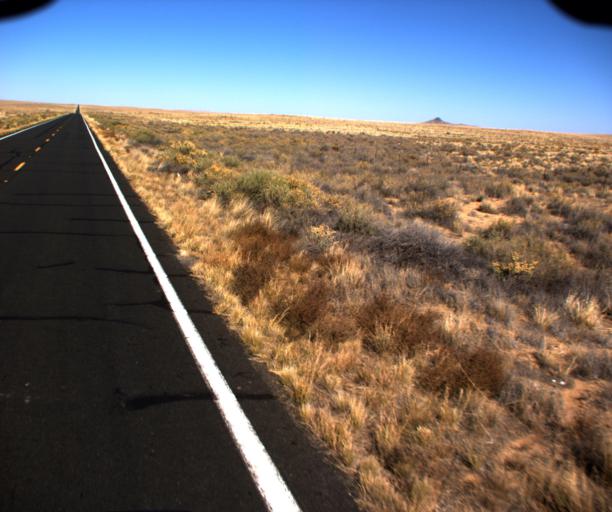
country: US
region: Arizona
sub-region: Navajo County
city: Dilkon
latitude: 35.5807
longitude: -110.4638
